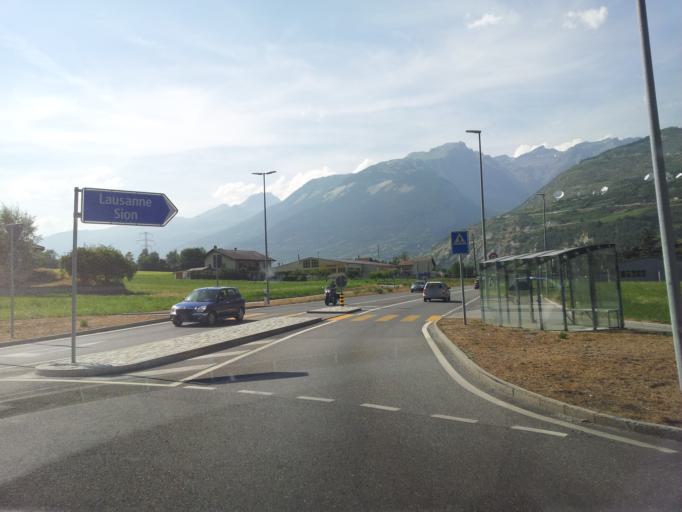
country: CH
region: Valais
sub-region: Leuk District
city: Leuk
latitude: 46.3009
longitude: 7.6585
